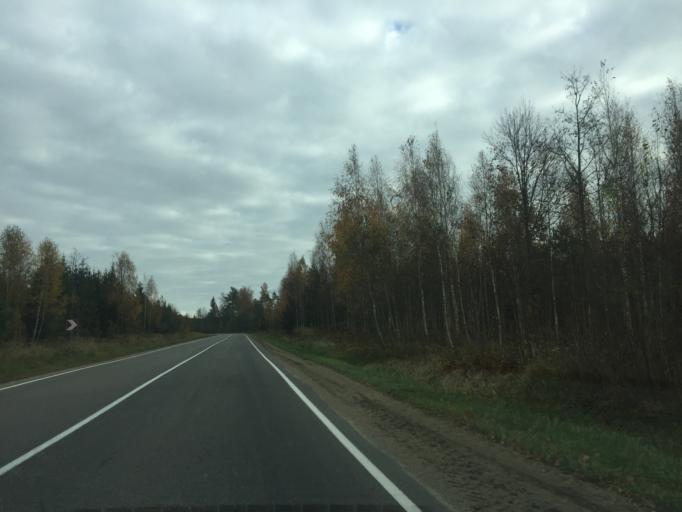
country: BY
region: Minsk
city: Svir
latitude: 54.8497
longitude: 26.2370
